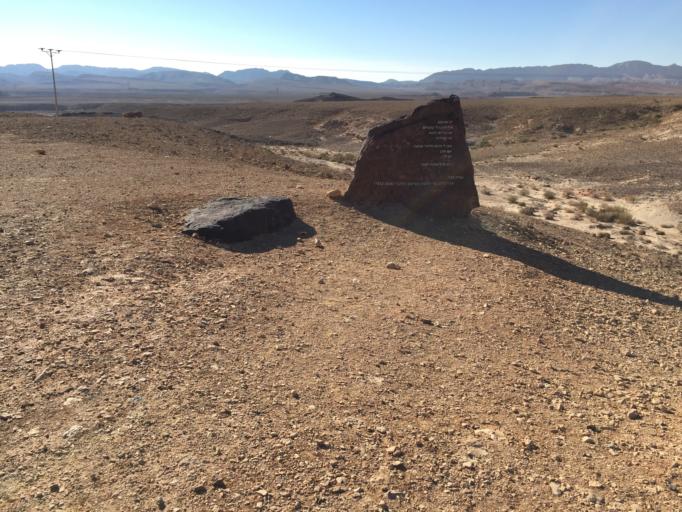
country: IL
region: Southern District
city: Mitzpe Ramon
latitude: 30.6164
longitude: 34.8476
